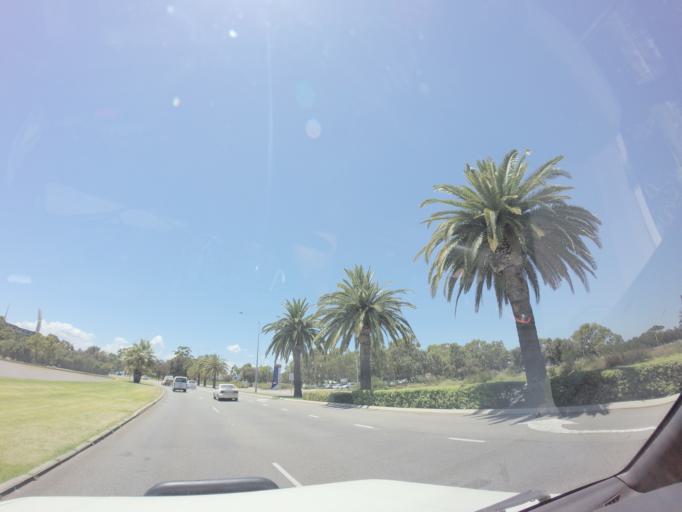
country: AU
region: Western Australia
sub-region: City of Perth
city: East Perth
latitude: -31.9638
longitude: 115.8766
